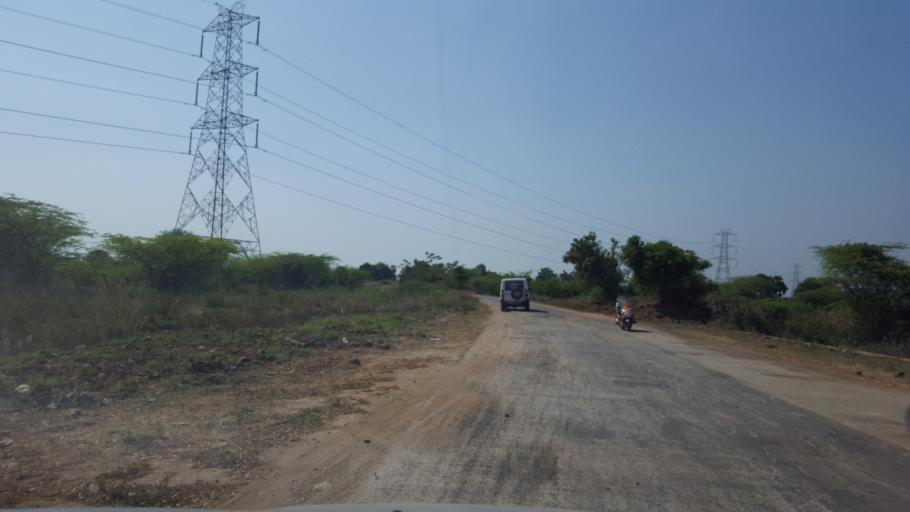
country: IN
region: Tamil Nadu
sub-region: Kancheepuram
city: Wallajahbad
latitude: 12.8595
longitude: 79.7922
